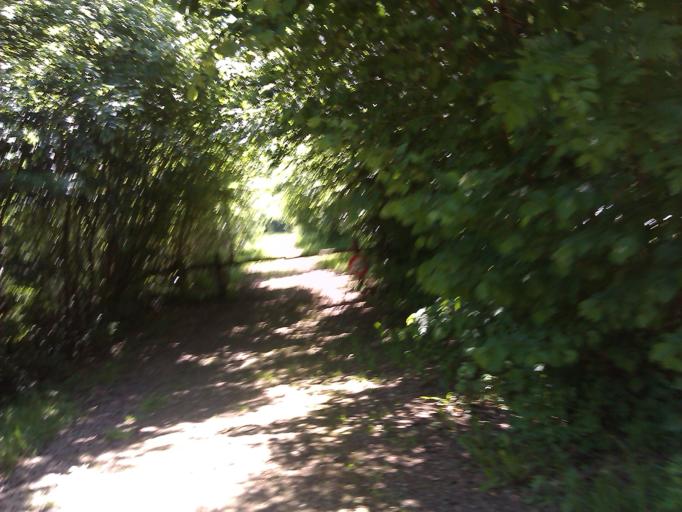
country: FR
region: Centre
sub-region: Departement de l'Indre
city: Saint-Gaultier
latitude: 46.6427
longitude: 1.3152
